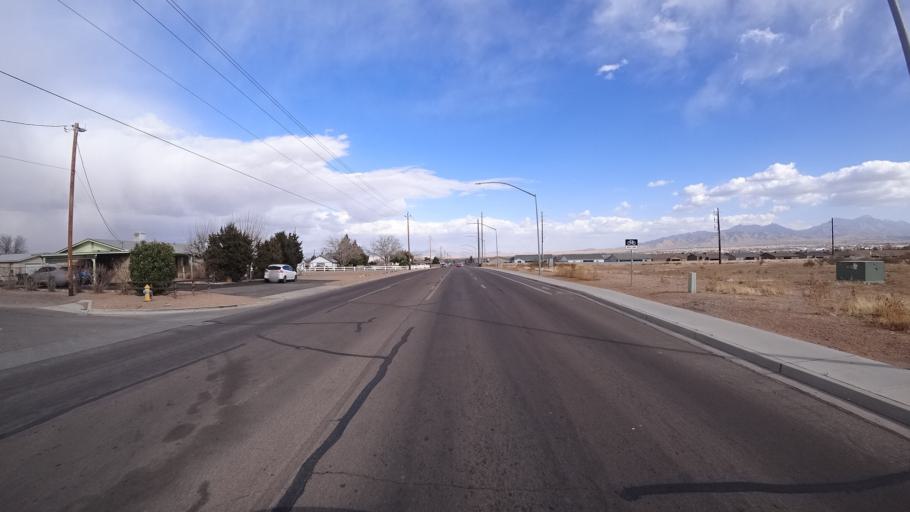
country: US
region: Arizona
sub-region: Mohave County
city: New Kingman-Butler
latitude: 35.2394
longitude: -114.0351
